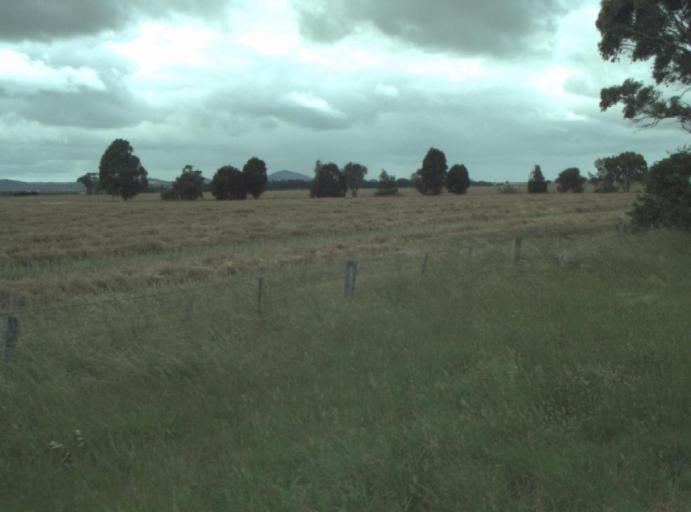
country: AU
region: Victoria
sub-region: Greater Geelong
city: Lara
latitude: -37.8578
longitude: 144.3523
